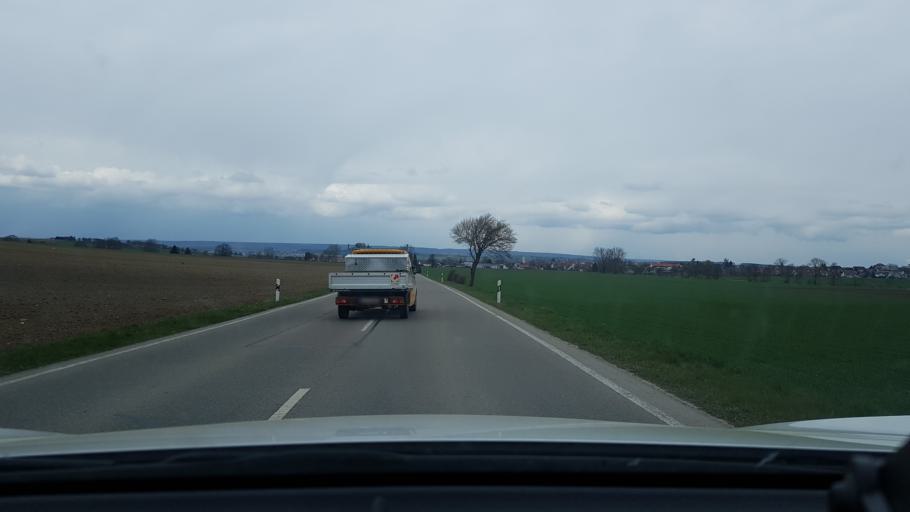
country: DE
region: Baden-Wuerttemberg
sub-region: Tuebingen Region
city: Oberstadion
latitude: 48.1906
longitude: 9.6907
